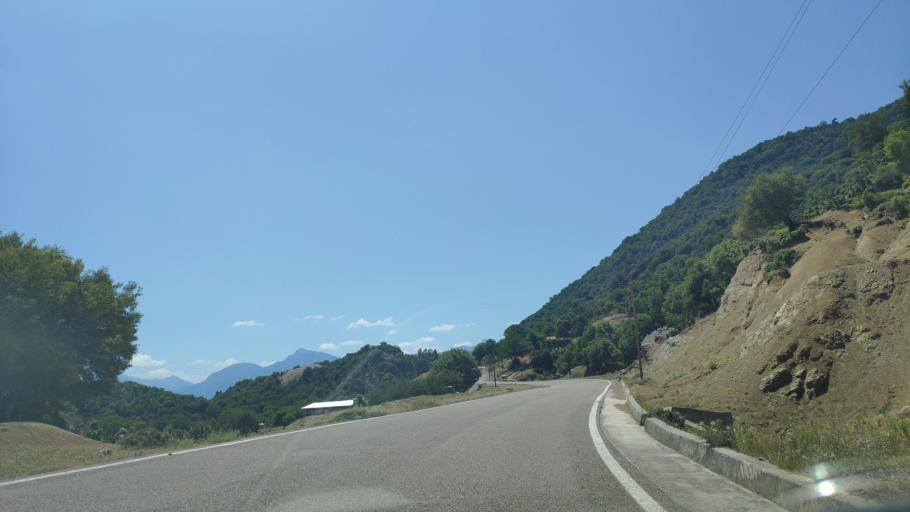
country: GR
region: Central Greece
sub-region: Nomos Evrytanias
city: Kerasochori
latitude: 38.9647
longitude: 21.4616
